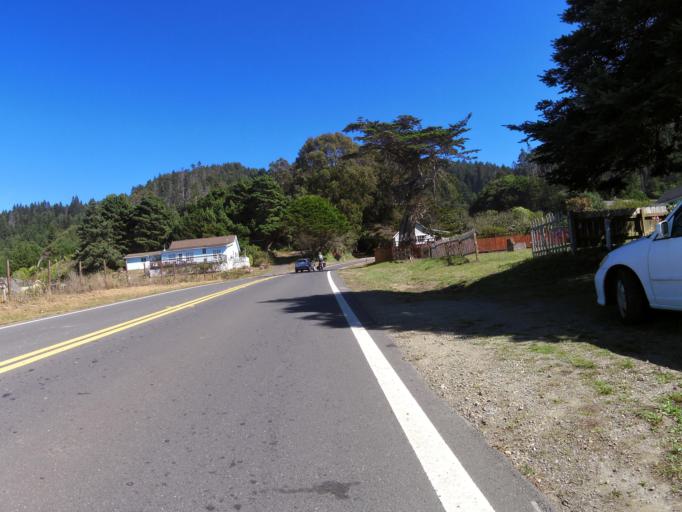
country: US
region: California
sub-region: Mendocino County
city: Fort Bragg
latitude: 39.6357
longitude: -123.7840
